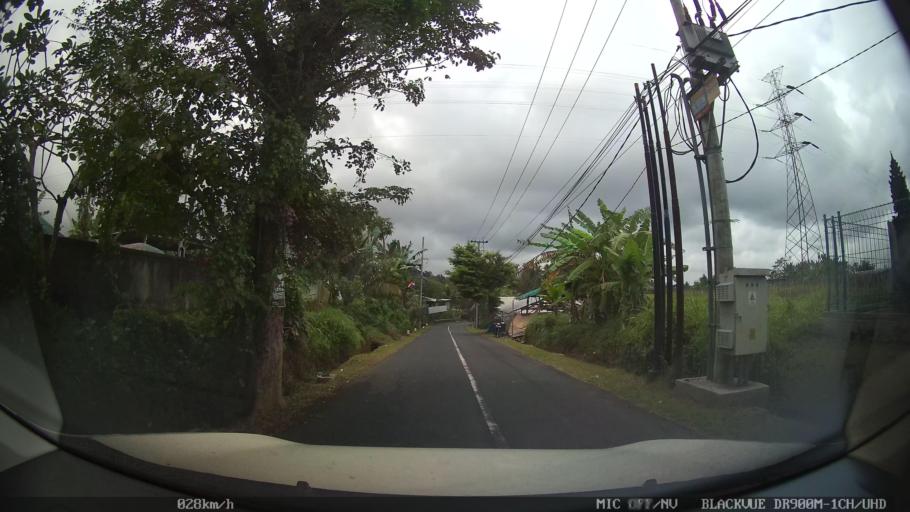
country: ID
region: Bali
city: Banjar Tengahbelayu
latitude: -8.5245
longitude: 115.1817
